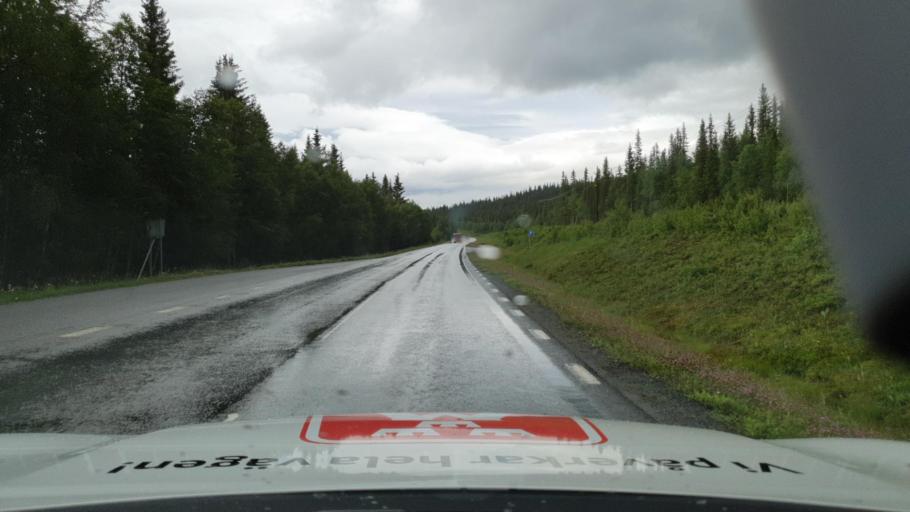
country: SE
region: Vaesterbotten
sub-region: Vilhelmina Kommun
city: Sjoberg
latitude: 65.5769
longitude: 15.5299
